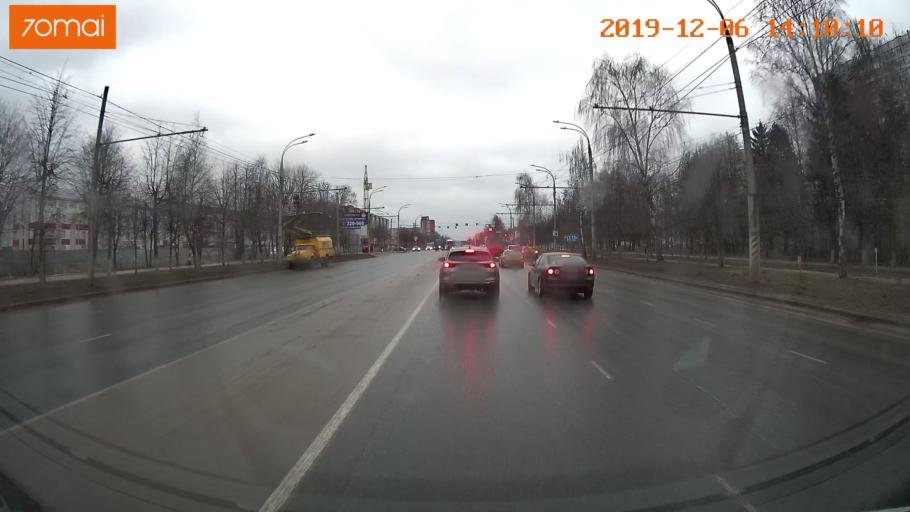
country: RU
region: Ivanovo
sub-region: Gorod Ivanovo
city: Ivanovo
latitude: 56.9628
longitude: 40.9736
